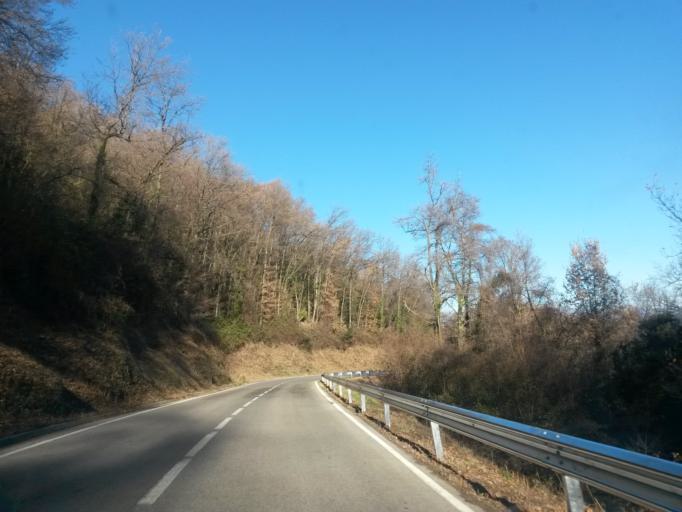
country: ES
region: Catalonia
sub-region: Provincia de Girona
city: Sant Feliu de Pallerols
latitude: 42.0692
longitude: 2.4942
